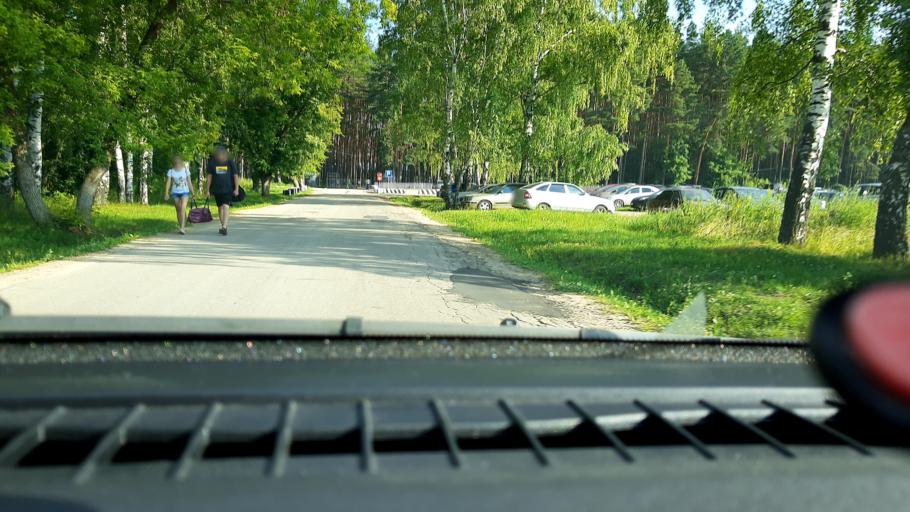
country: RU
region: Nizjnij Novgorod
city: Babino
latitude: 56.1427
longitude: 43.6507
